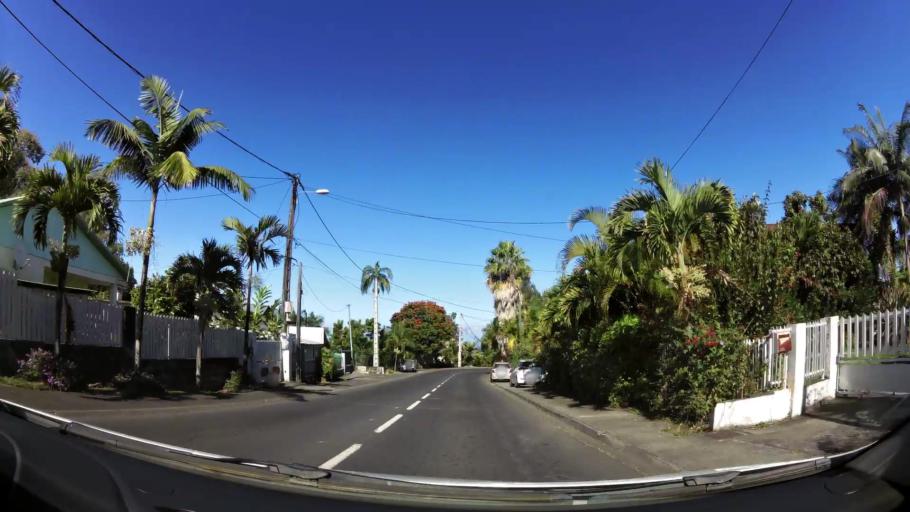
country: RE
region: Reunion
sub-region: Reunion
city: Le Tampon
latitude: -21.2808
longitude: 55.5257
